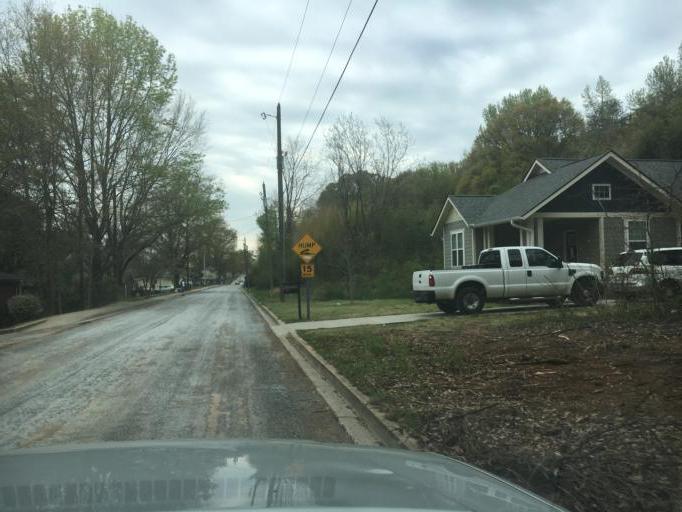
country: US
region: South Carolina
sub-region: Greenville County
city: Greenville
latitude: 34.8612
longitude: -82.3765
